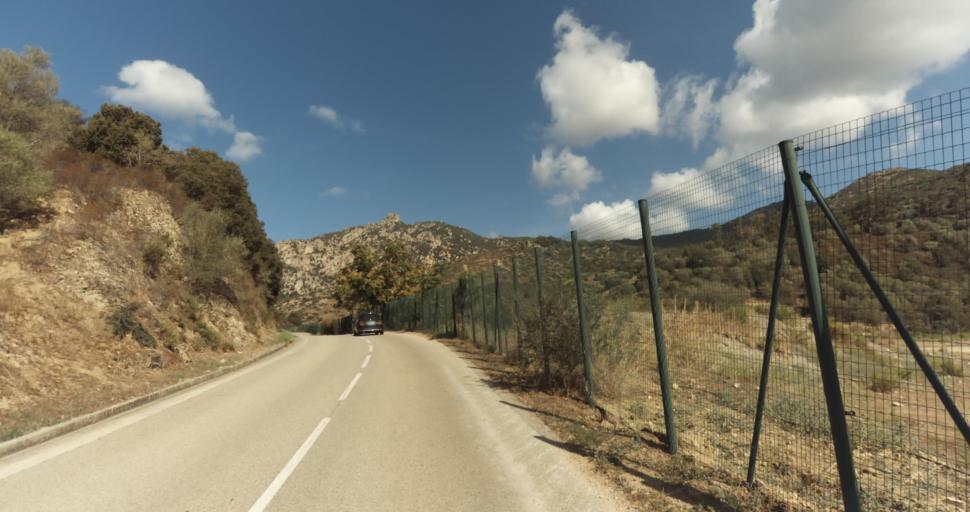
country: FR
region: Corsica
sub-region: Departement de la Corse-du-Sud
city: Ajaccio
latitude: 41.9303
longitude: 8.6941
